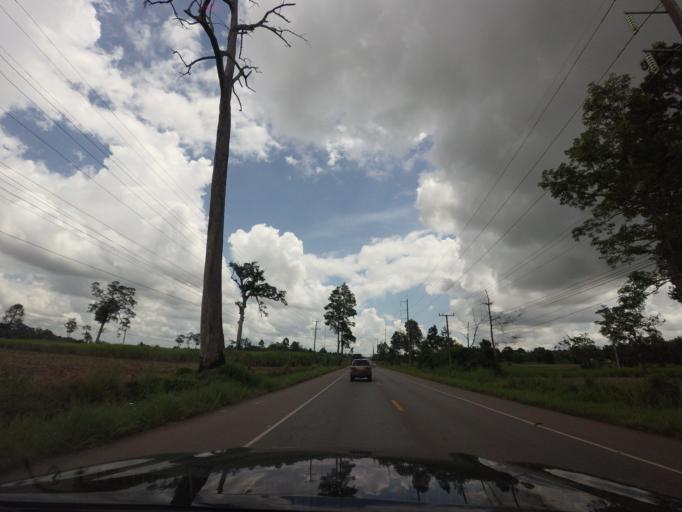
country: TH
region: Changwat Udon Thani
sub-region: Amphoe Ban Phue
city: Ban Phue
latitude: 17.5916
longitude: 102.5997
